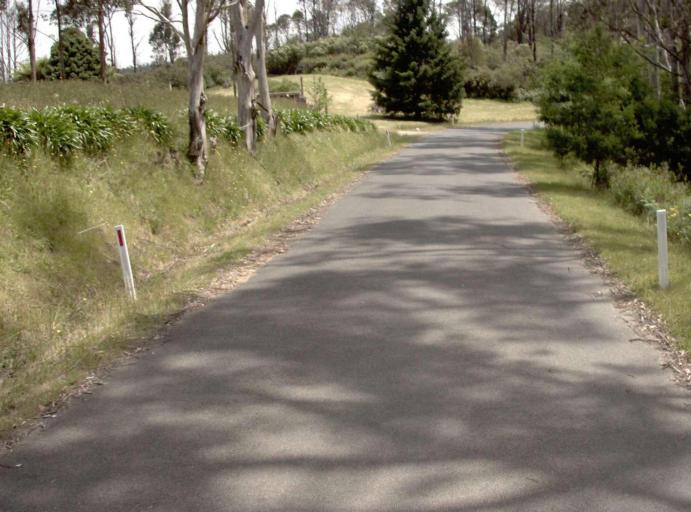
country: AU
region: Victoria
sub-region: Latrobe
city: Traralgon
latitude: -38.4302
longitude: 146.5381
